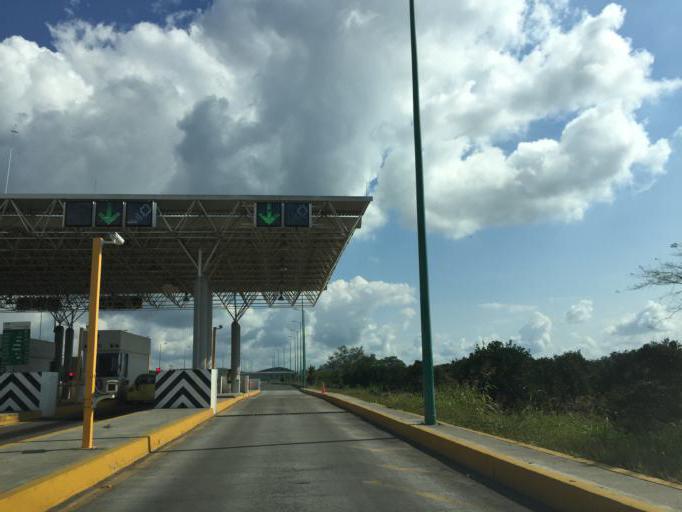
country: MX
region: Veracruz
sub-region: Tihuatlan
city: La Isla (Kilometro 10)
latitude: 20.6107
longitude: -97.6147
